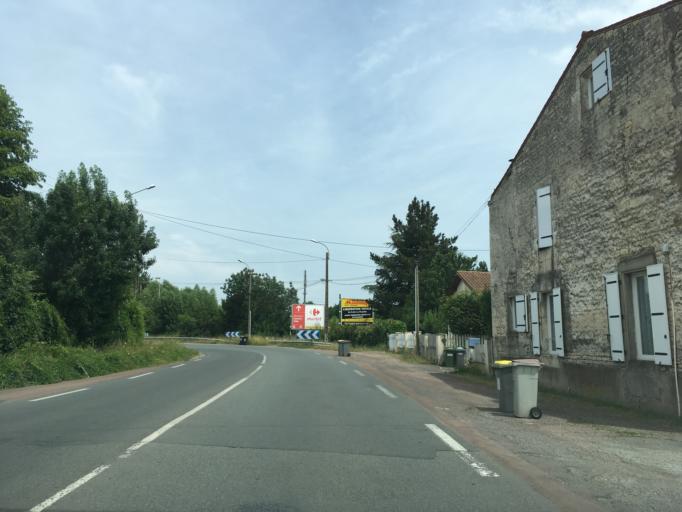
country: FR
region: Poitou-Charentes
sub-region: Departement des Deux-Sevres
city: Niort
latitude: 46.3054
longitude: -0.4651
